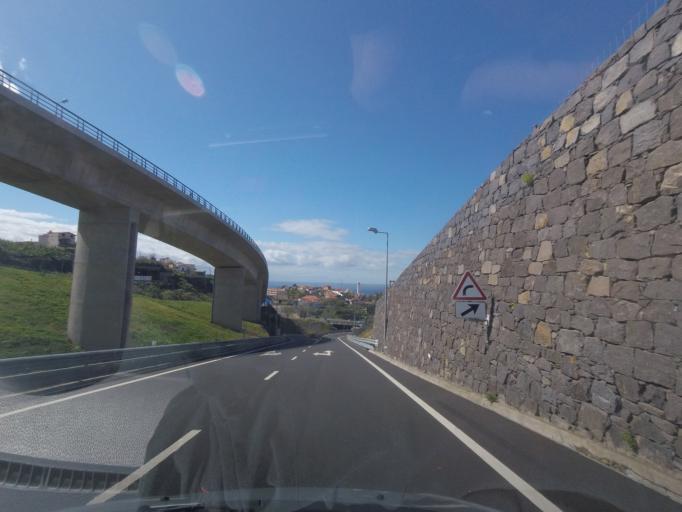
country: PT
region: Madeira
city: Camara de Lobos
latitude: 32.6597
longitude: -16.9699
